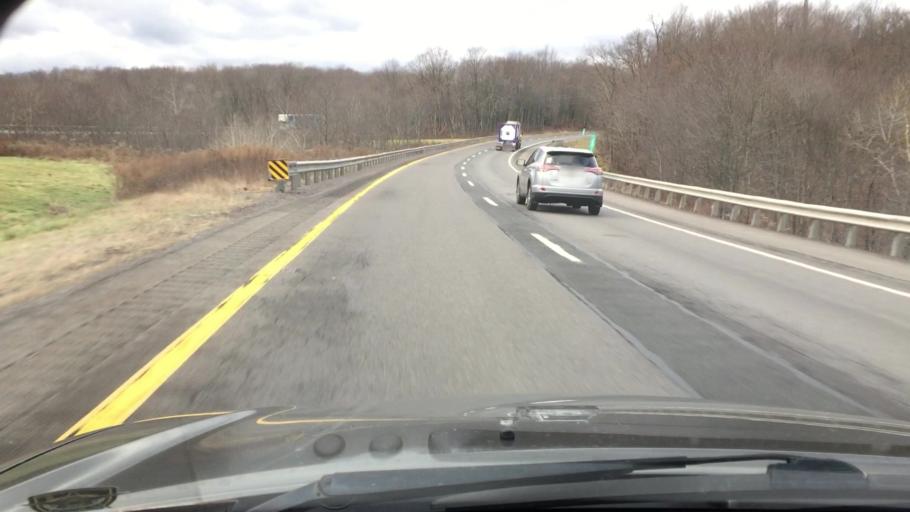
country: US
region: Pennsylvania
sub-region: Carbon County
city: Towamensing Trails
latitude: 41.0792
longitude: -75.6100
